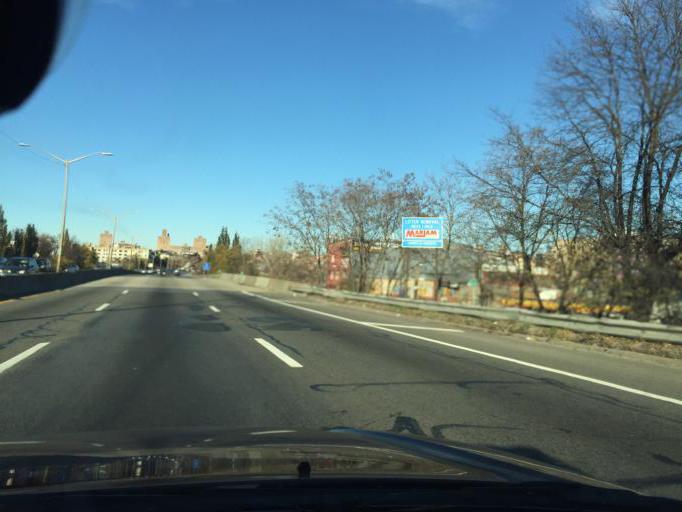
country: US
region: New York
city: New York City
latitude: 40.6975
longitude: -73.9625
